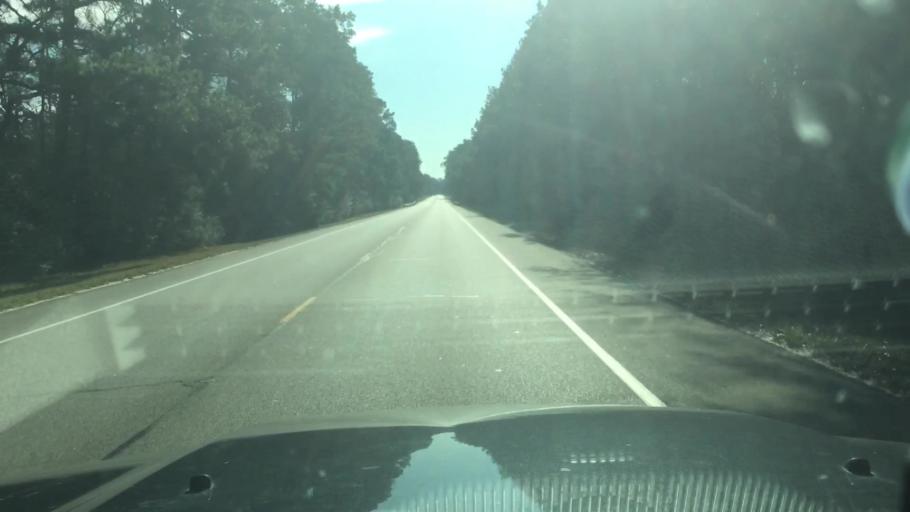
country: US
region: Texas
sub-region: Montgomery County
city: Porter Heights
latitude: 30.2337
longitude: -95.3726
